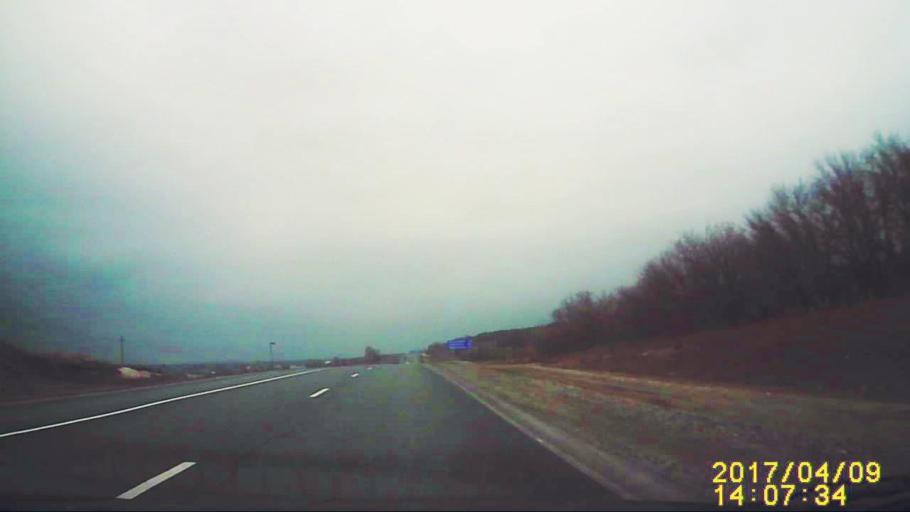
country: RU
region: Ulyanovsk
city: Silikatnyy
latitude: 54.0125
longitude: 48.2178
